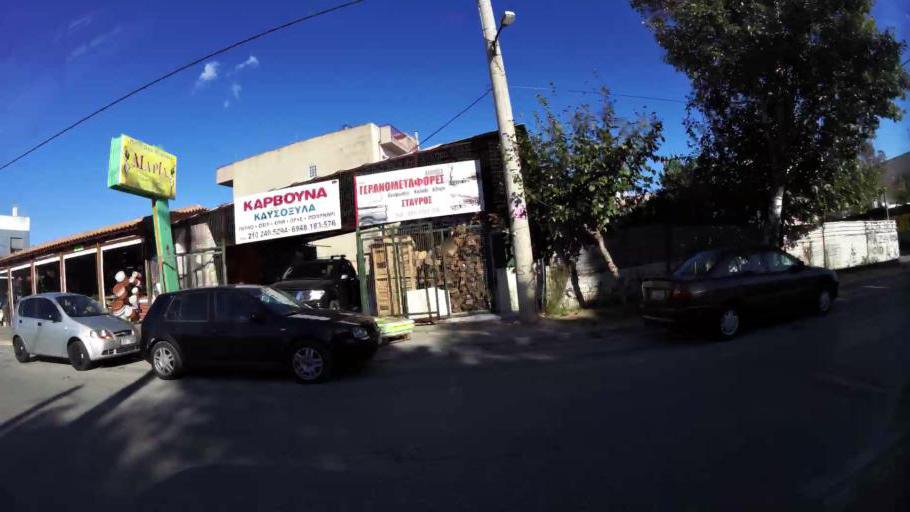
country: GR
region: Attica
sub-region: Nomarchia Anatolikis Attikis
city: Acharnes
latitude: 38.0915
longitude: 23.7262
